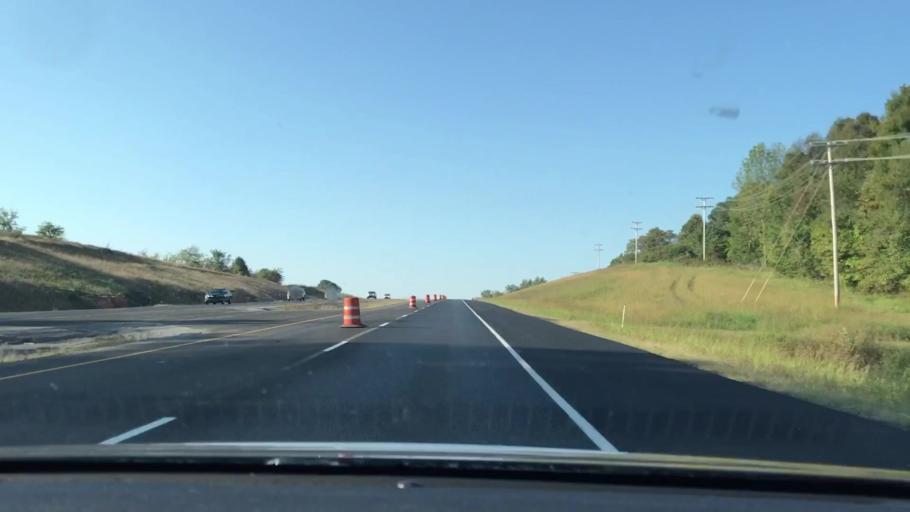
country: US
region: Kentucky
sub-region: Trigg County
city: Cadiz
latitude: 36.8504
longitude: -87.8193
